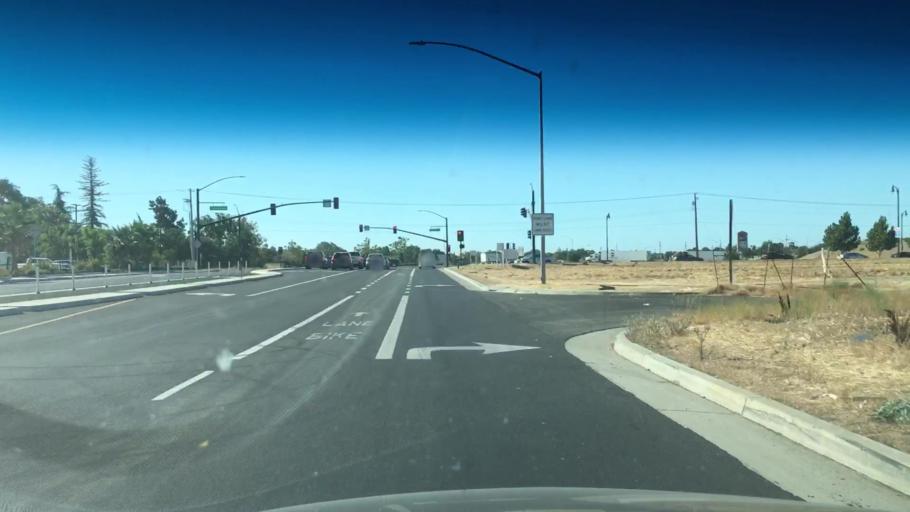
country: US
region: California
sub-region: Sacramento County
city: Laguna
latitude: 38.4392
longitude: -121.3974
